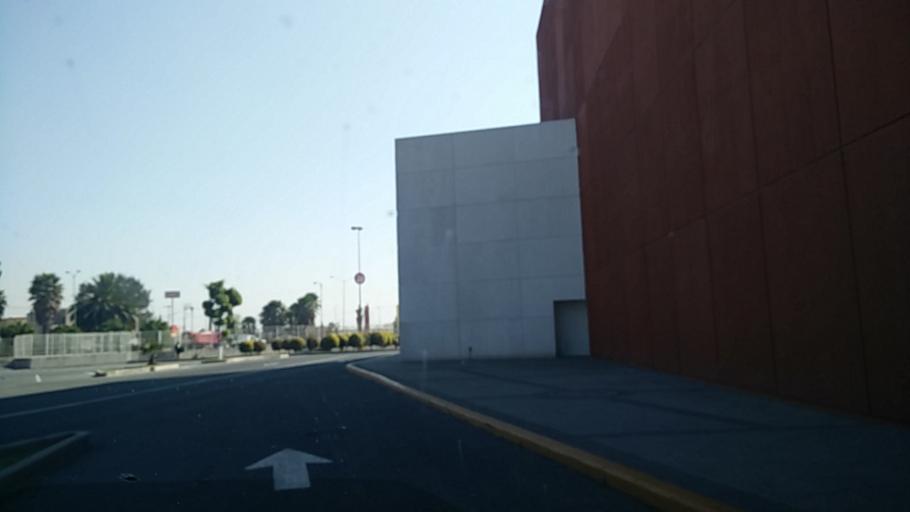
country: MX
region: Mexico
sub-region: Atenco
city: Colonia el Salado
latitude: 19.5856
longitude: -99.0238
